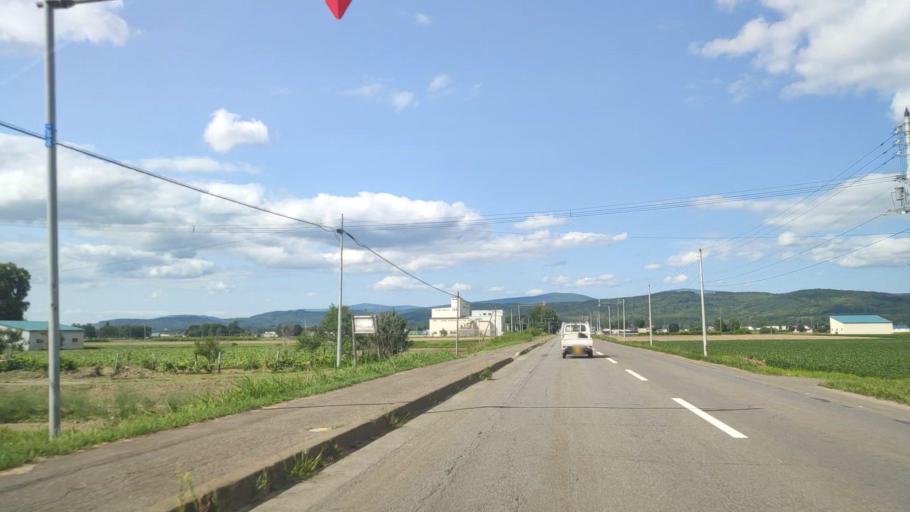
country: JP
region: Hokkaido
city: Nayoro
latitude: 44.4293
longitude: 142.4001
